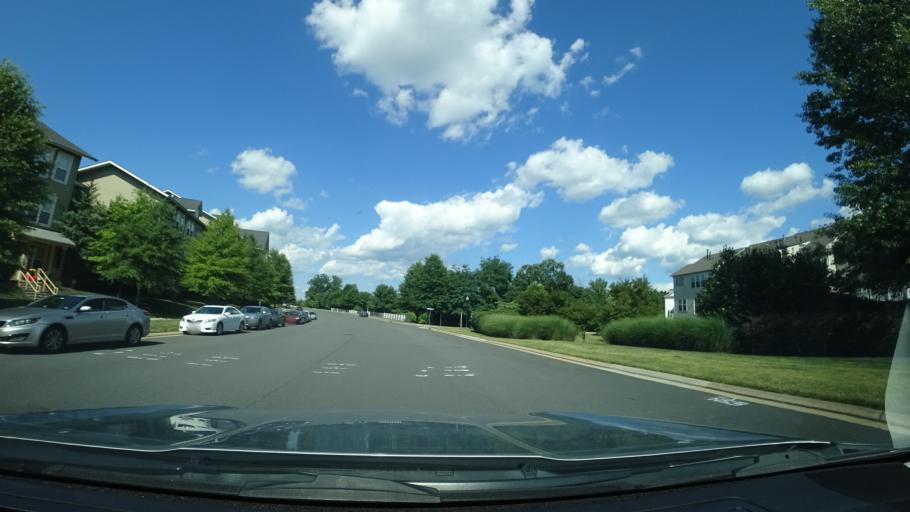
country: US
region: Virginia
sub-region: Loudoun County
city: Broadlands
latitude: 38.9902
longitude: -77.4842
